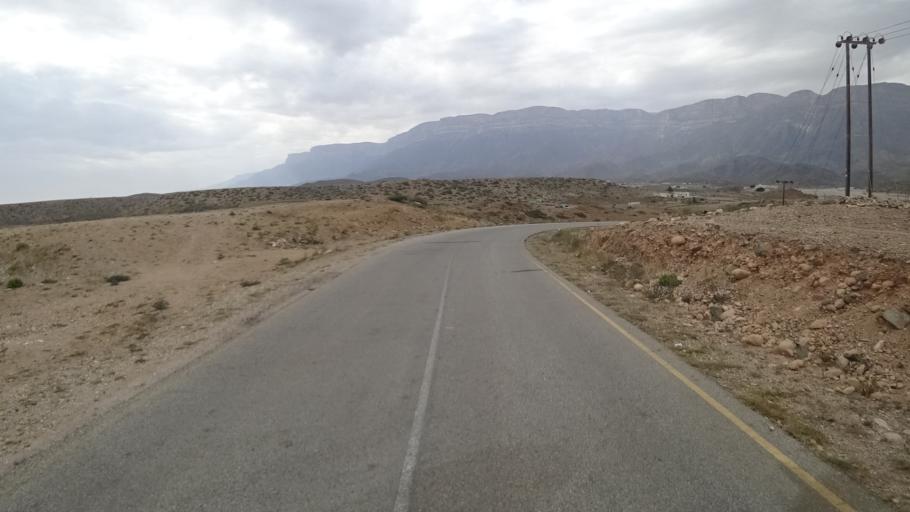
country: OM
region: Zufar
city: Salalah
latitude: 17.1558
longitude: 54.9976
